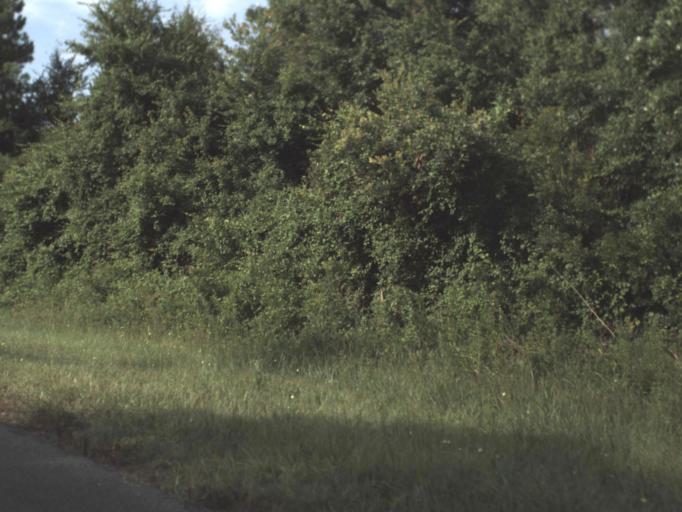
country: US
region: Florida
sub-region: Taylor County
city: Perry
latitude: 30.2707
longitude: -83.6279
